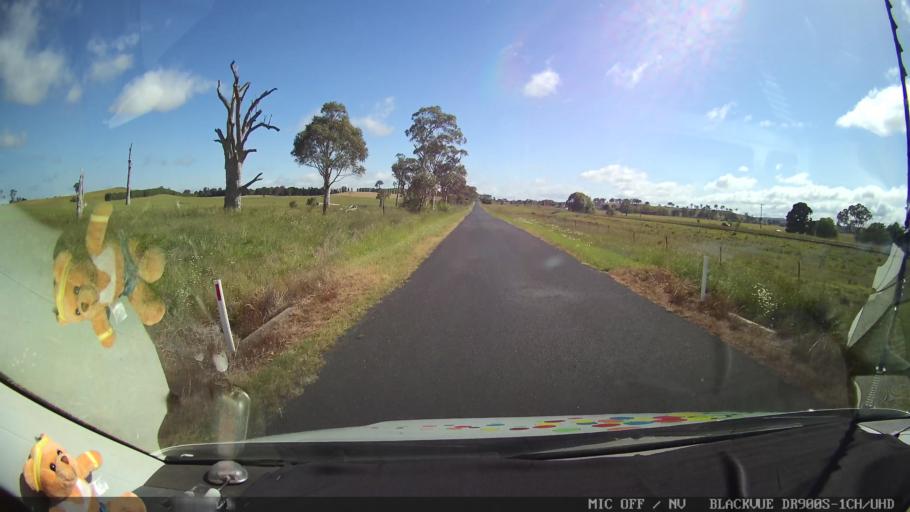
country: AU
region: New South Wales
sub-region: Guyra
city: Guyra
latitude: -30.1834
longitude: 151.6793
